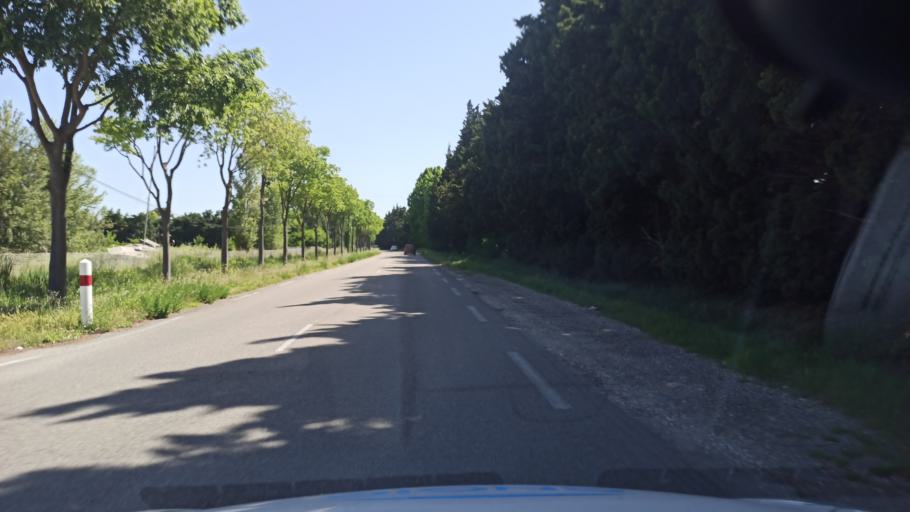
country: FR
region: Provence-Alpes-Cote d'Azur
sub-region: Departement des Bouches-du-Rhone
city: Saint-Andiol
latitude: 43.8429
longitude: 4.9262
